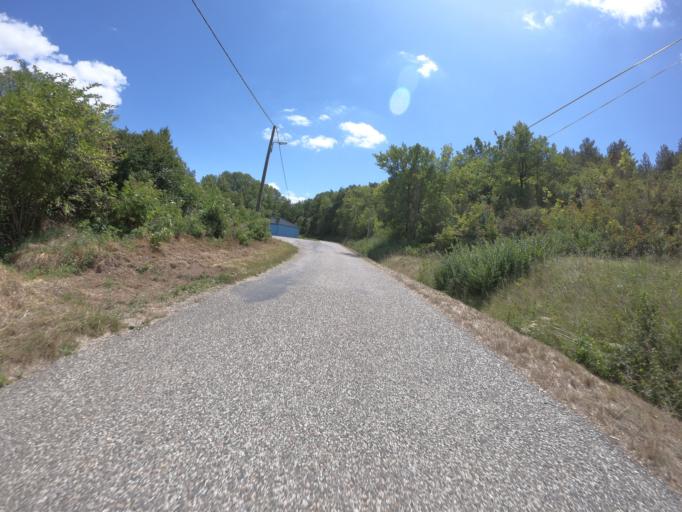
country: FR
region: Midi-Pyrenees
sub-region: Departement de l'Ariege
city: Mirepoix
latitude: 43.0756
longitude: 1.8389
